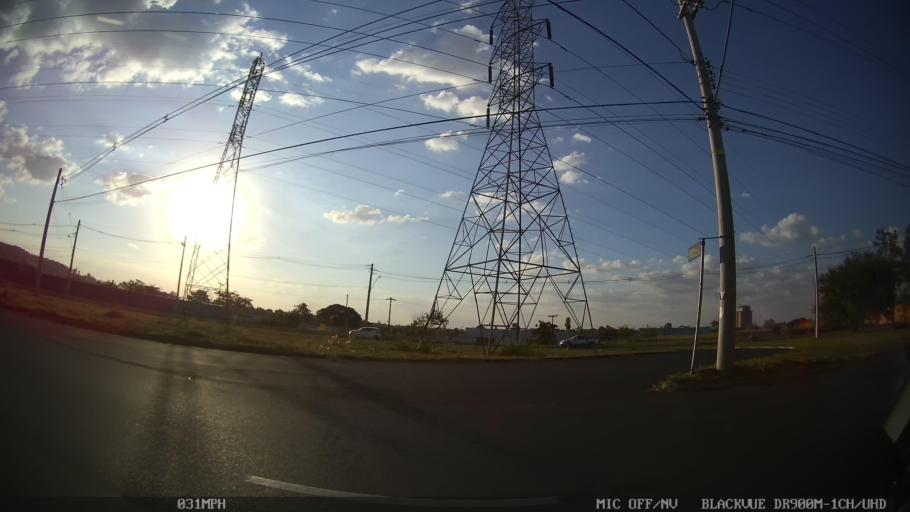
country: BR
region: Sao Paulo
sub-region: Ribeirao Preto
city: Ribeirao Preto
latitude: -21.1684
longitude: -47.7539
